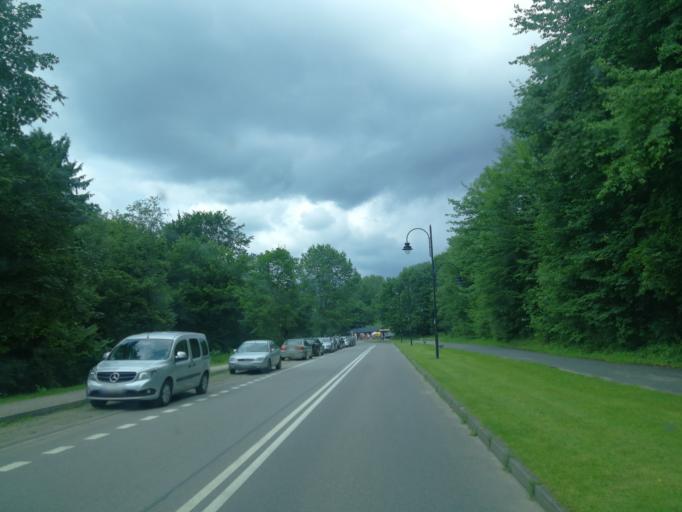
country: PL
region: Subcarpathian Voivodeship
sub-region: Powiat leski
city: Polanczyk
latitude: 49.3764
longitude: 22.4429
